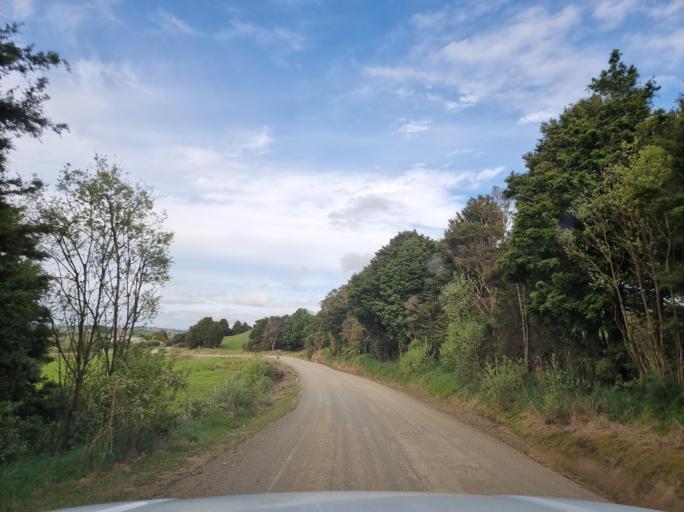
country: NZ
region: Northland
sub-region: Whangarei
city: Ruakaka
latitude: -36.0821
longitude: 174.3684
